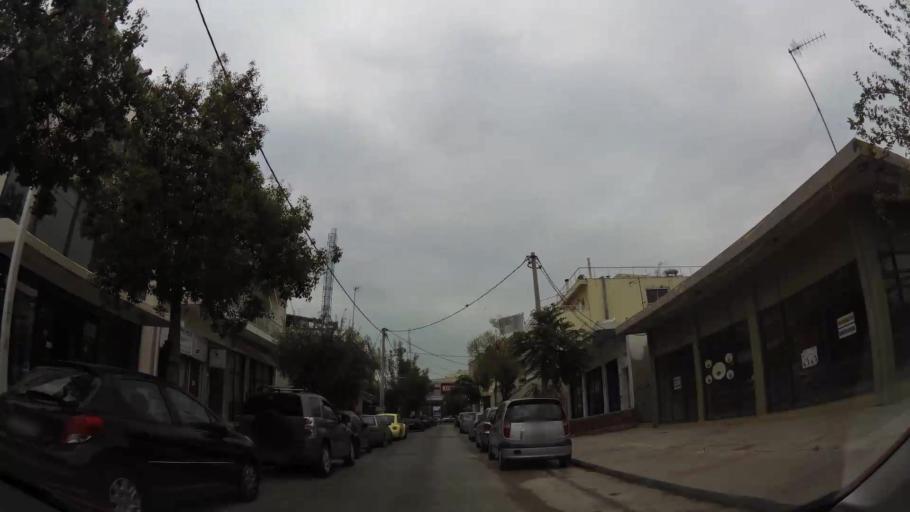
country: GR
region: Attica
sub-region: Nomarchia Athinas
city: Ilion
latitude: 38.0296
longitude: 23.7015
